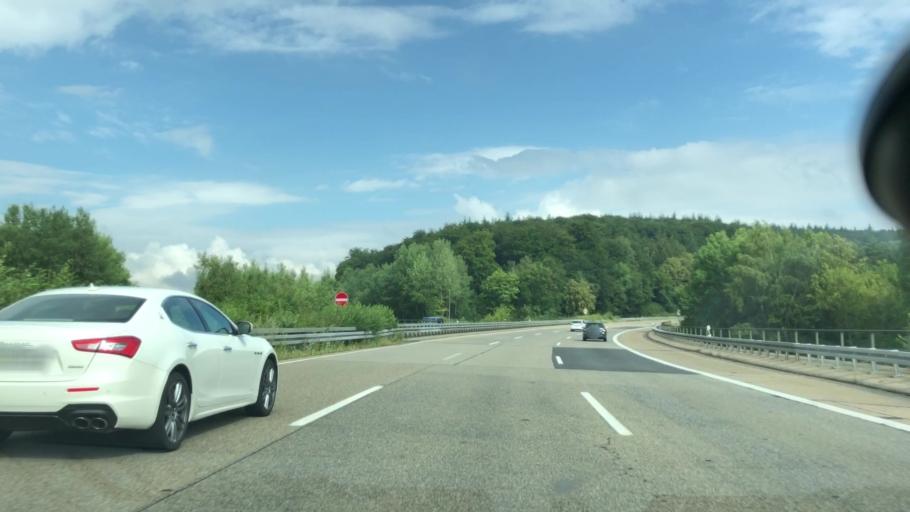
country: DE
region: Hesse
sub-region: Regierungsbezirk Kassel
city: Kirchheim
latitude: 50.8005
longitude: 9.5368
